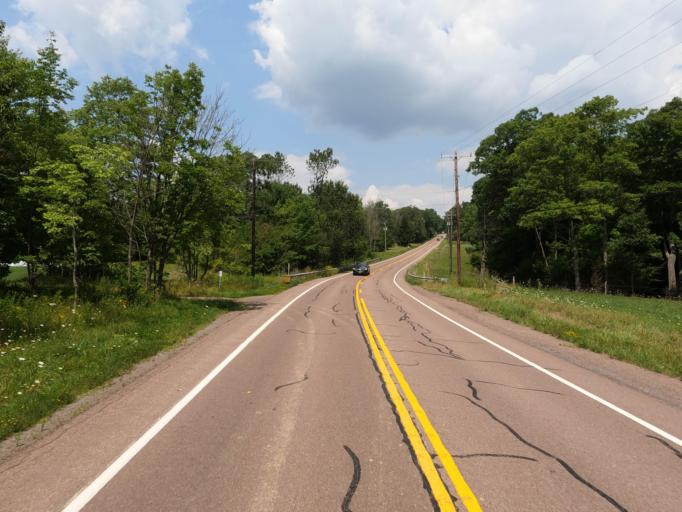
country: US
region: Maryland
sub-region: Allegany County
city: Westernport
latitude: 39.6288
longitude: -79.2146
